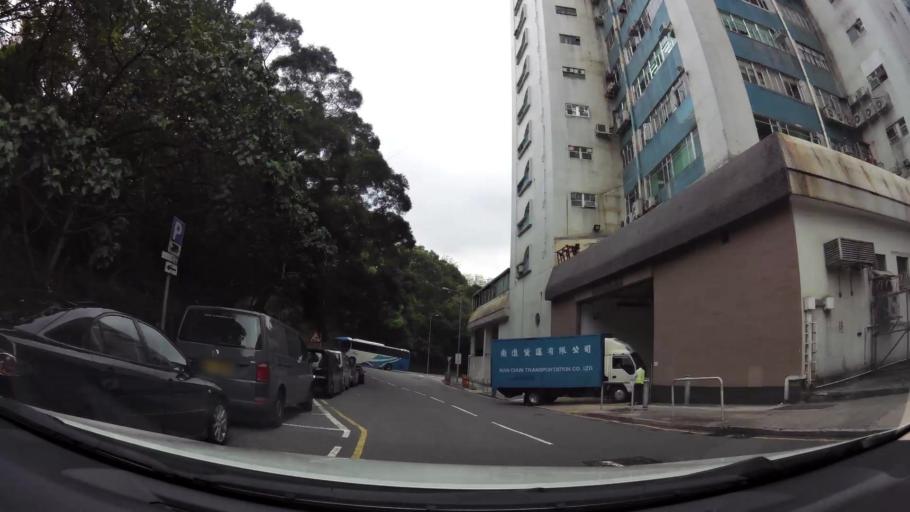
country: HK
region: Sha Tin
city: Sha Tin
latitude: 22.3998
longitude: 114.1947
